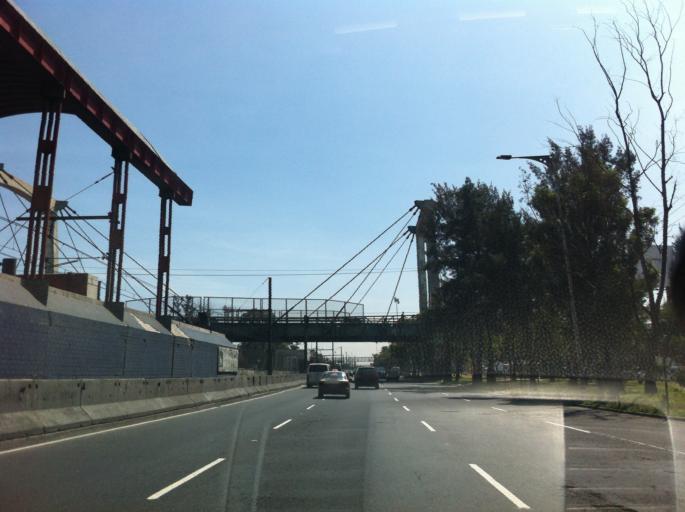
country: MX
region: Mexico City
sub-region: Iztacalco
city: Iztacalco
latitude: 19.3984
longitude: -99.0591
